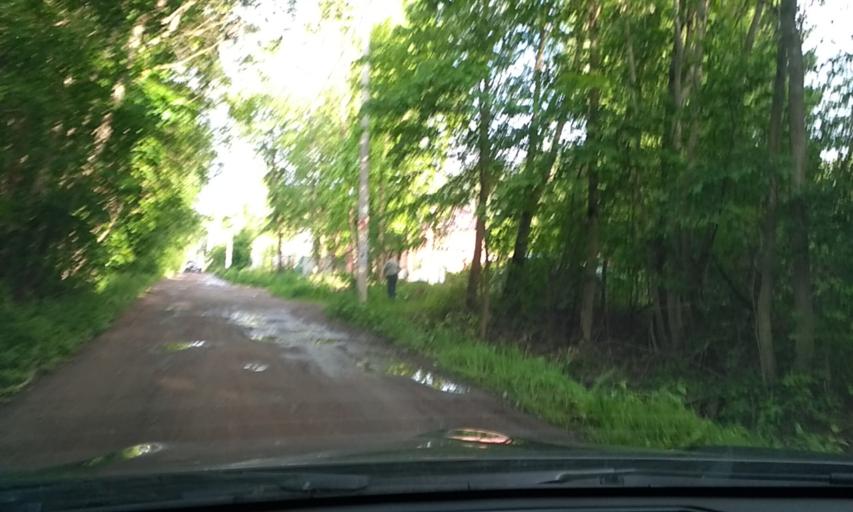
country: RU
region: Leningrad
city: Otradnoye
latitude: 59.8072
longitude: 30.8109
